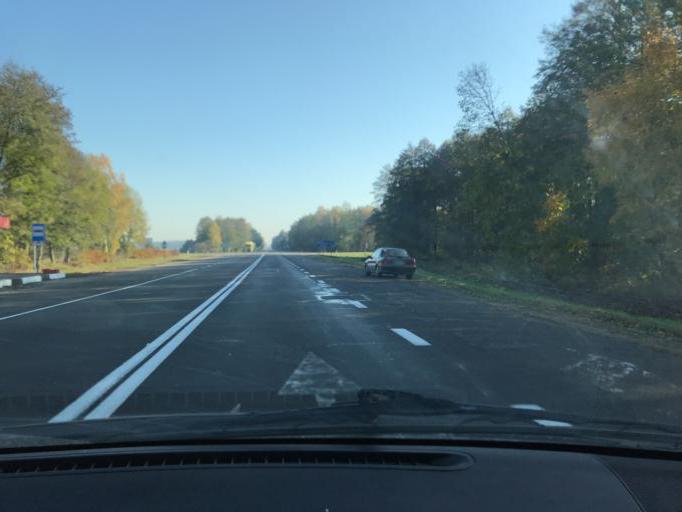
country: BY
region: Brest
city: Baranovichi
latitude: 52.9163
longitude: 25.9568
